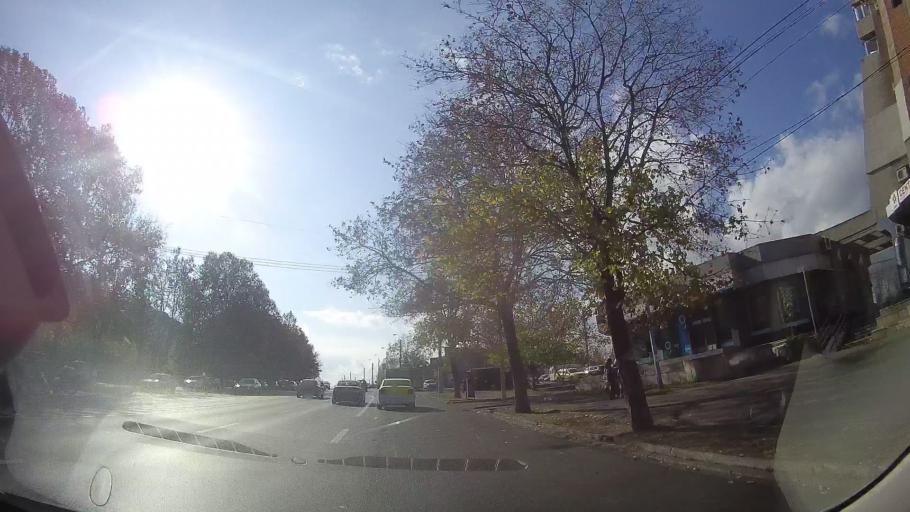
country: RO
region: Constanta
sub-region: Municipiul Constanta
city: Constanta
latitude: 44.1550
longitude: 28.6292
